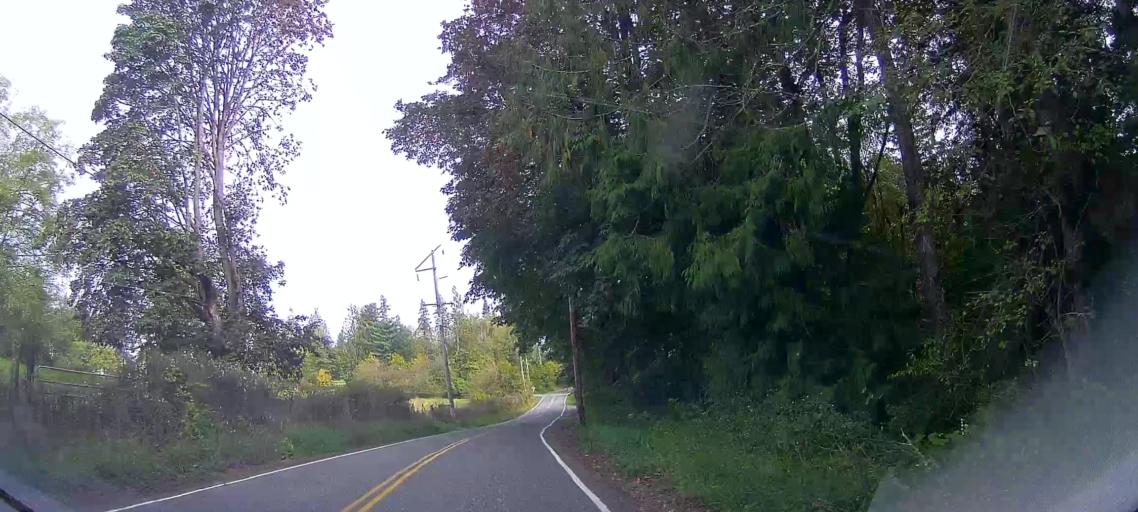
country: US
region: Washington
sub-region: Skagit County
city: Burlington
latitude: 48.4537
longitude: -122.2888
